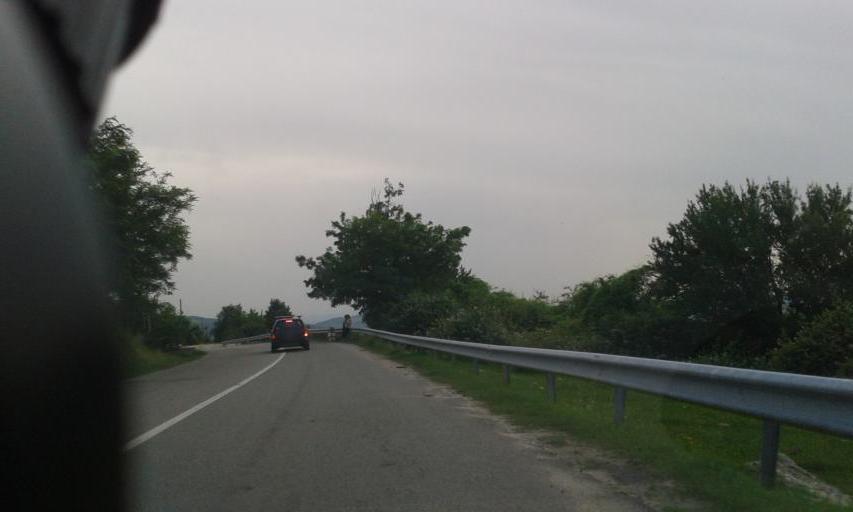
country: RO
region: Gorj
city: Novaci-Straini
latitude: 45.1885
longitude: 23.6822
